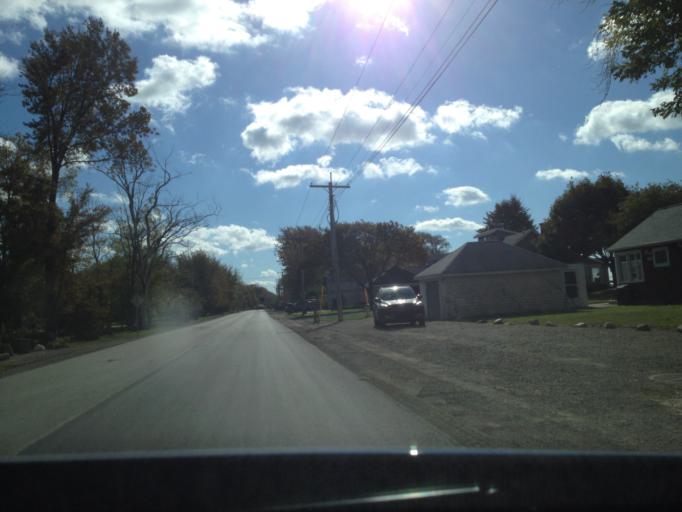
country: CA
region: Ontario
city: Amherstburg
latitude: 42.0063
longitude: -82.5682
